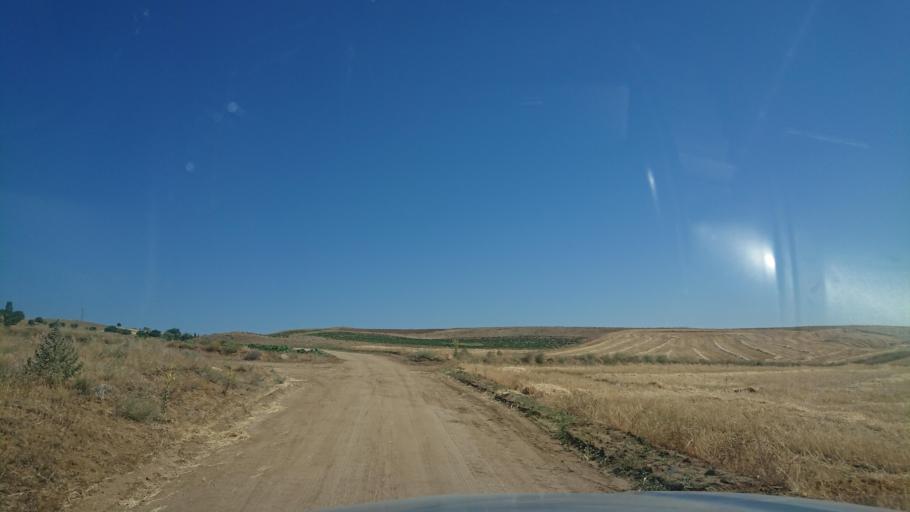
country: TR
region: Aksaray
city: Agacoren
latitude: 38.9030
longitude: 33.9008
